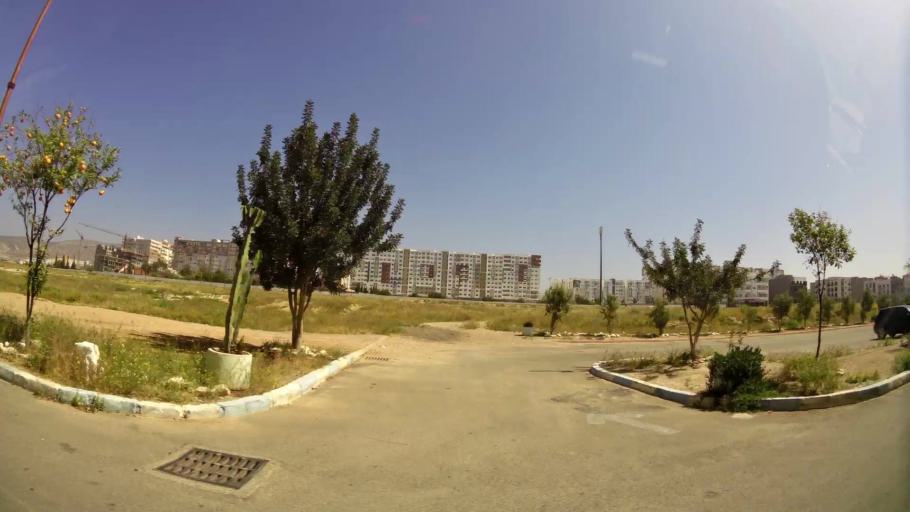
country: MA
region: Oued ed Dahab-Lagouira
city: Dakhla
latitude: 30.4323
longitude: -9.5646
